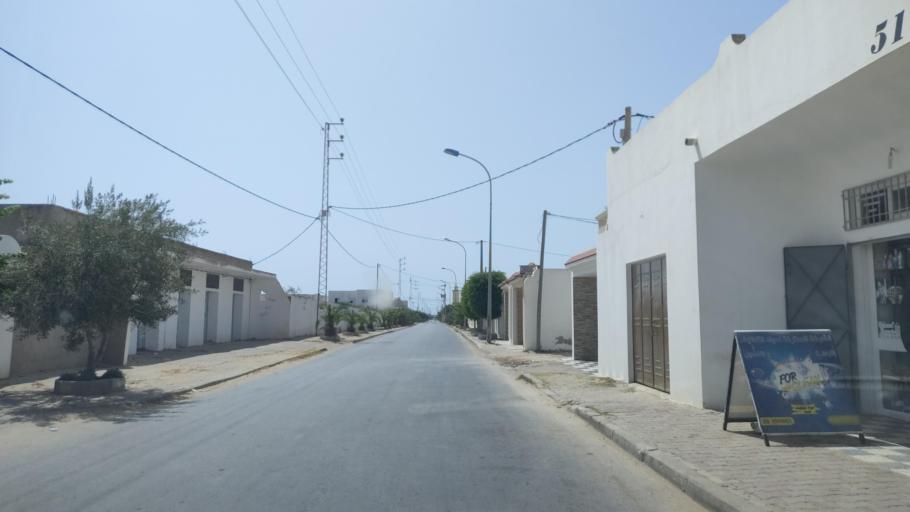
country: TN
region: Safaqis
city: Sfax
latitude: 34.6764
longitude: 10.6992
